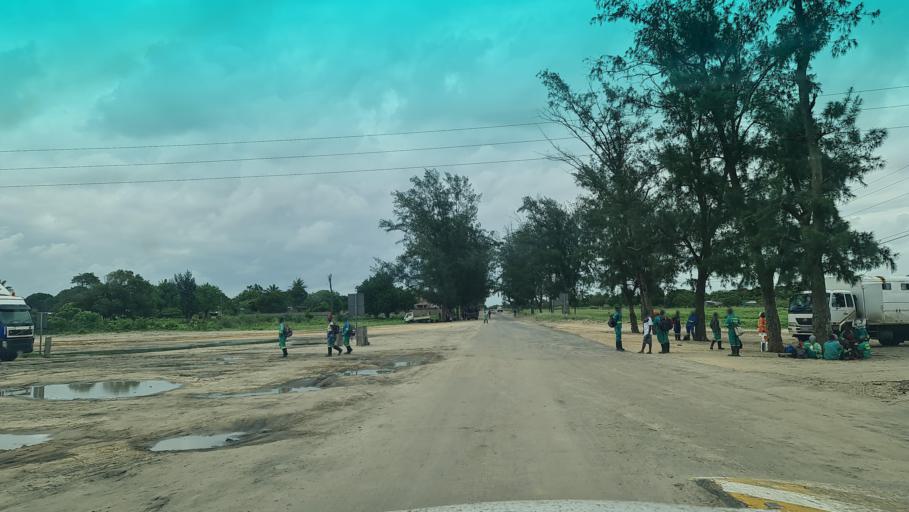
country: MZ
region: Maputo
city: Manhica
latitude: -25.4484
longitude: 32.7766
